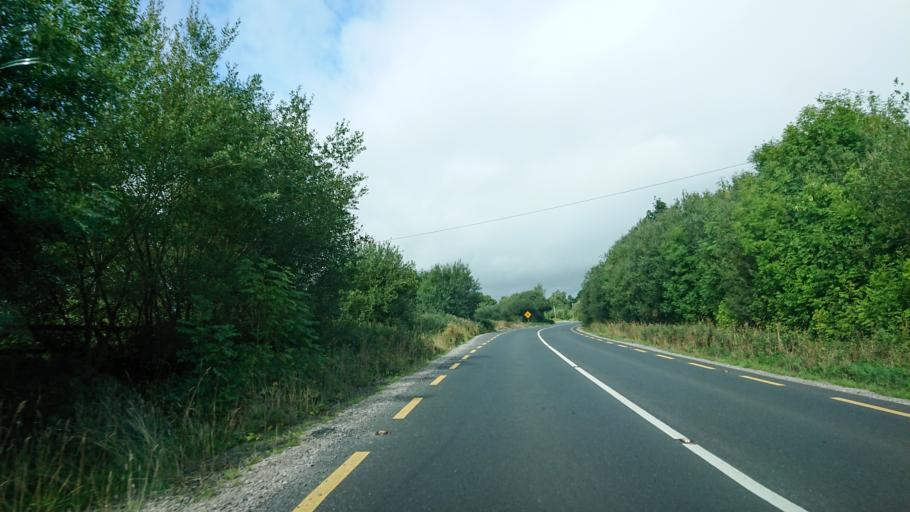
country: IE
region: Munster
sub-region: Ciarrai
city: Cill Airne
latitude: 52.0750
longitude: -9.6465
